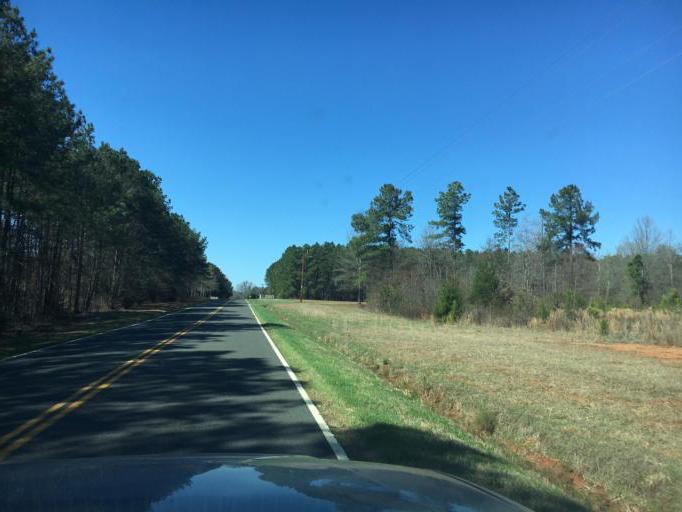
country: US
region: South Carolina
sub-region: Greenwood County
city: Ninety Six
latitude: 34.2774
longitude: -81.9473
